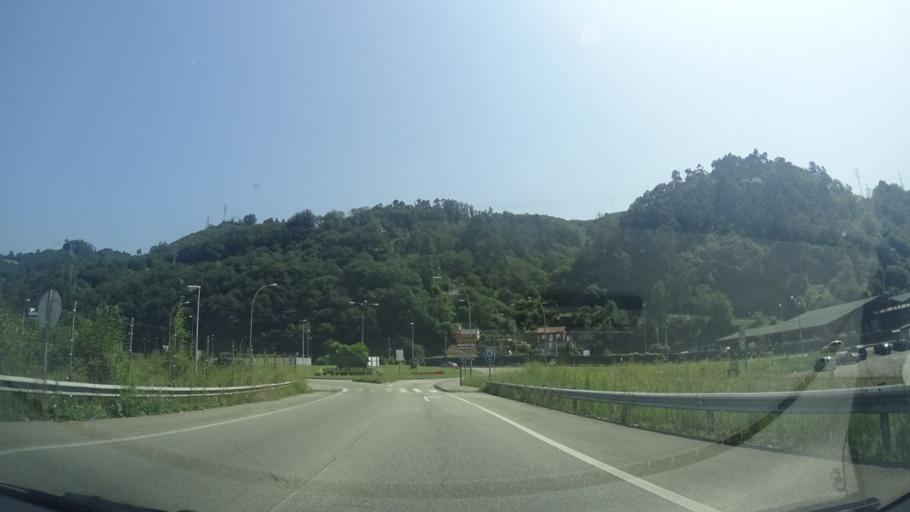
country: ES
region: Asturias
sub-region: Province of Asturias
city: Mieres
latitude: 43.2381
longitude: -5.7786
